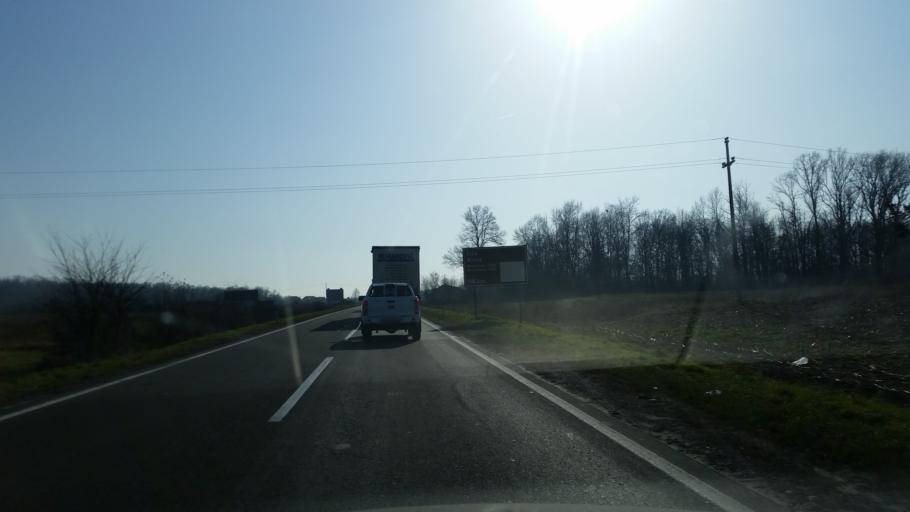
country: RS
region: Central Serbia
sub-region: Belgrade
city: Lazarevac
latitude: 44.3281
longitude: 20.2203
